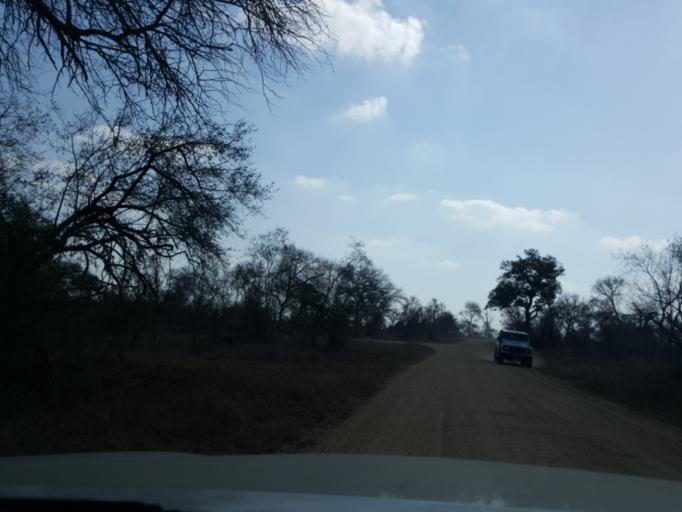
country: ZA
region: Mpumalanga
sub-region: Ehlanzeni District
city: Komatipoort
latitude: -25.2677
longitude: 31.7981
